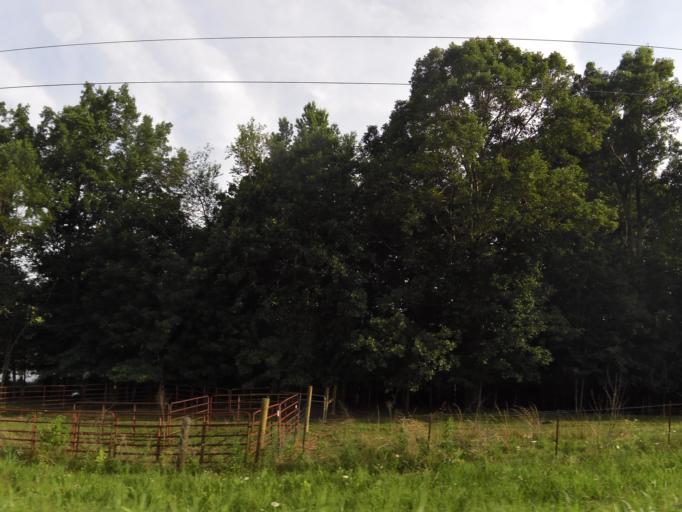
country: US
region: Tennessee
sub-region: Humphreys County
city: McEwen
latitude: 36.0946
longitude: -87.5704
